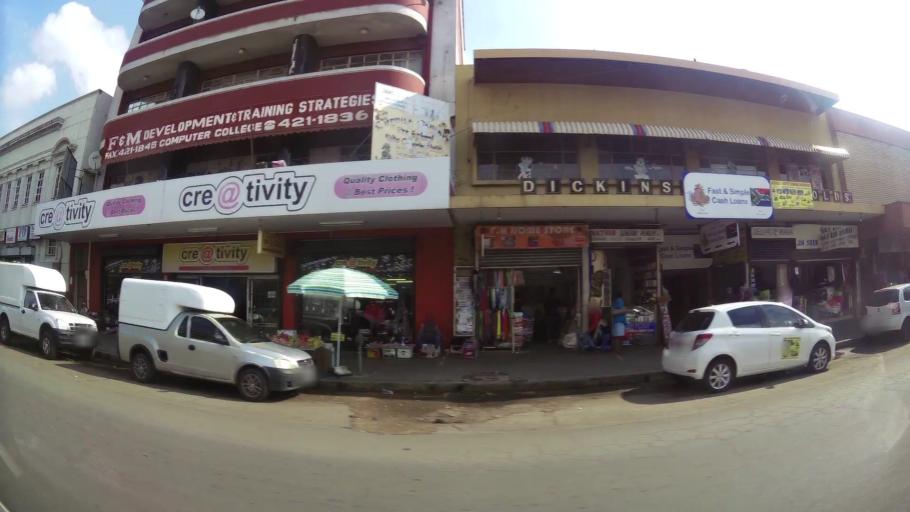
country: ZA
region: Gauteng
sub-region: Sedibeng District Municipality
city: Vereeniging
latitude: -26.6744
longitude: 27.9315
